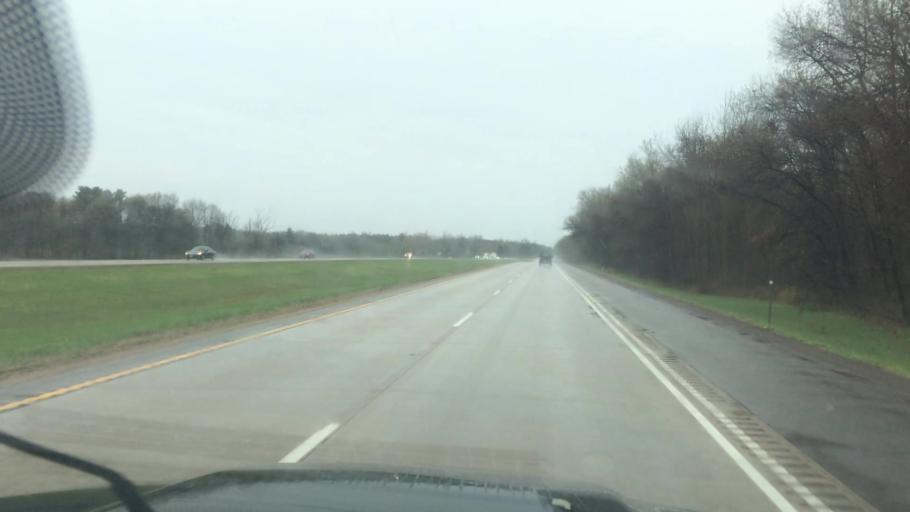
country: US
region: Wisconsin
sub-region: Portage County
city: Stevens Point
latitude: 44.6506
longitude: -89.6389
